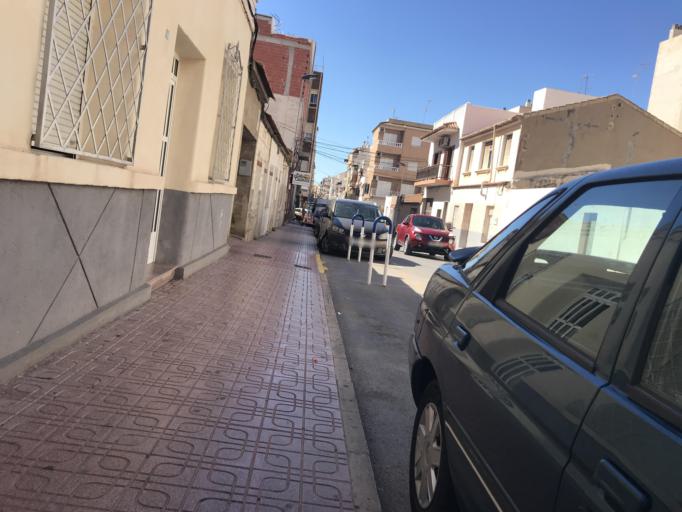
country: ES
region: Valencia
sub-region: Provincia de Alicante
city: Torrevieja
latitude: 37.9790
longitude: -0.6778
